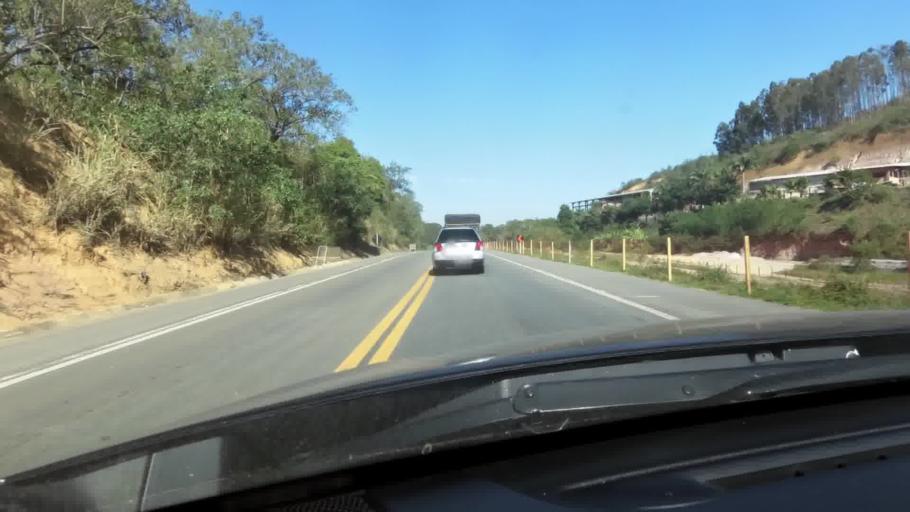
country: BR
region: Espirito Santo
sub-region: Rio Novo Do Sul
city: Rio Novo do Sul
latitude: -20.8967
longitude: -41.0091
